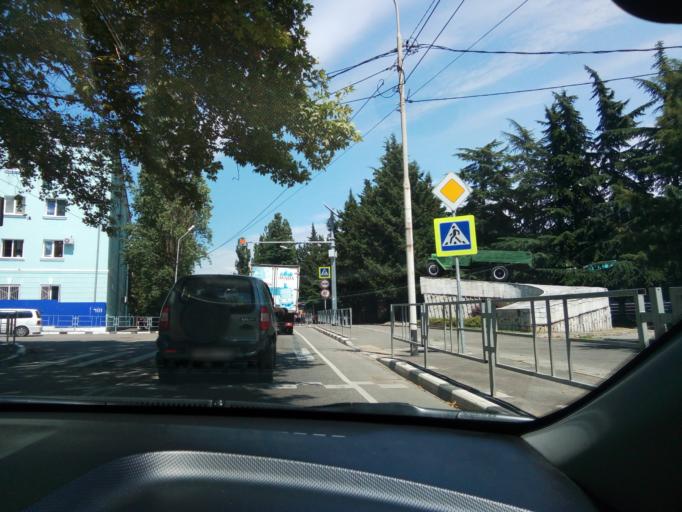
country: RU
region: Krasnodarskiy
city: Tuapse
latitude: 44.1100
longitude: 39.0938
